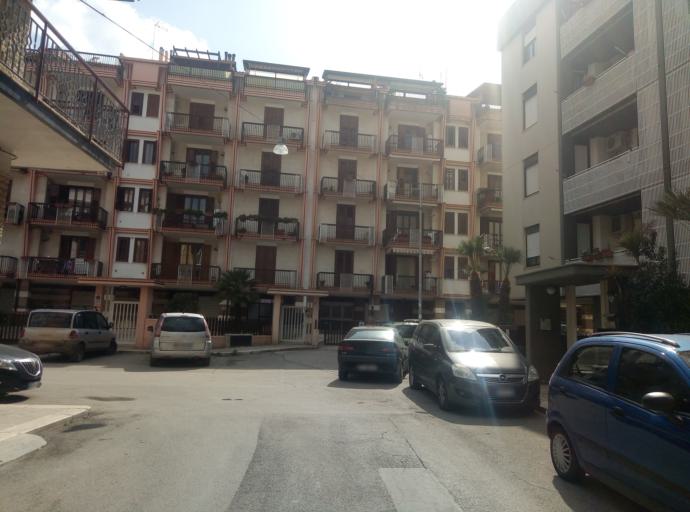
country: IT
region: Apulia
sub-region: Provincia di Bari
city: Ruvo di Puglia
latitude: 41.1171
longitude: 16.4790
